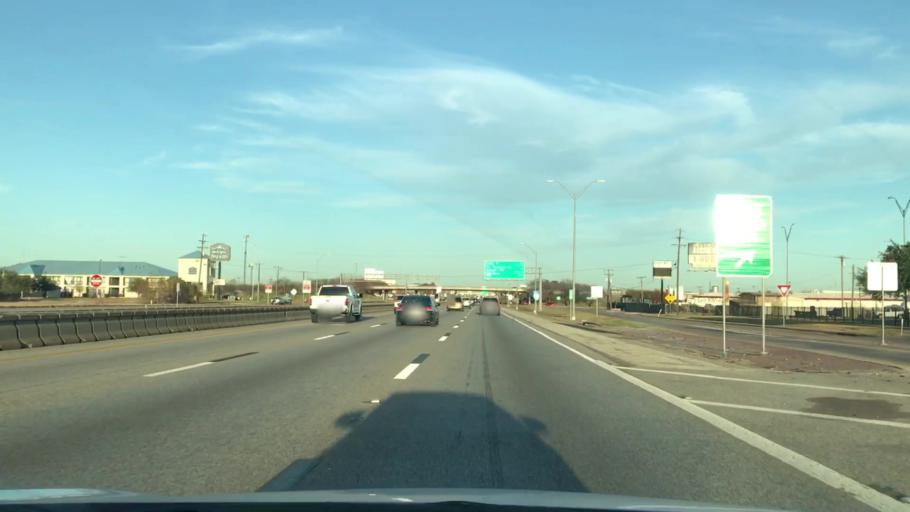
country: US
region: Texas
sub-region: Dallas County
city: Mesquite
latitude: 32.8020
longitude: -96.6718
